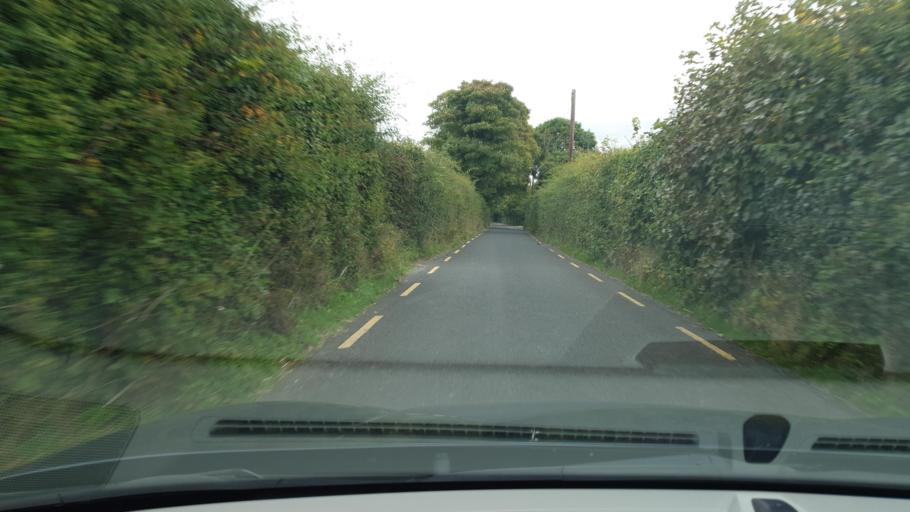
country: IE
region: Leinster
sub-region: Kildare
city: Clane
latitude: 53.2998
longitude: -6.7047
